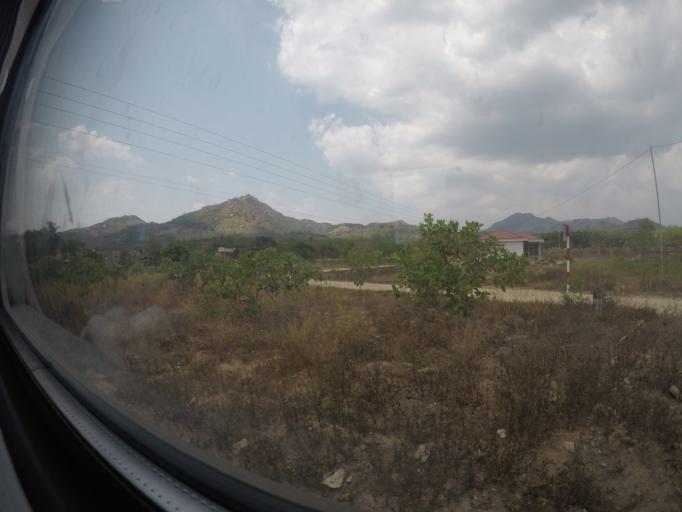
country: VN
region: Binh Thuan
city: Tanh Linh
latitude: 10.9666
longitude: 107.6327
